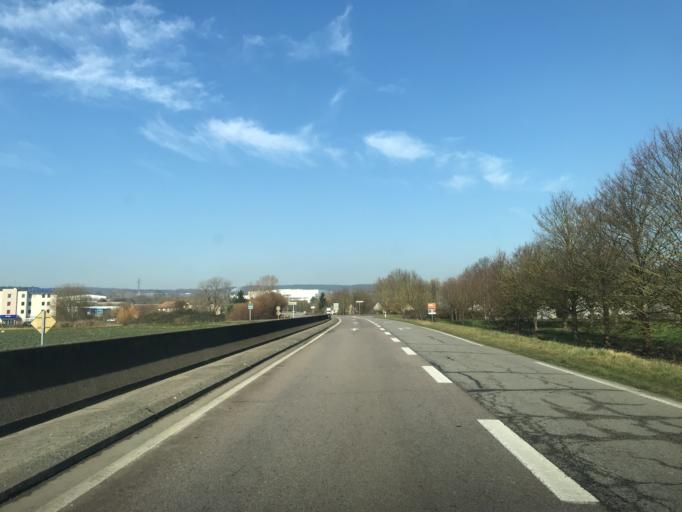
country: FR
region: Haute-Normandie
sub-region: Departement de l'Eure
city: Le Vaudreuil
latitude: 49.2475
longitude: 1.1910
